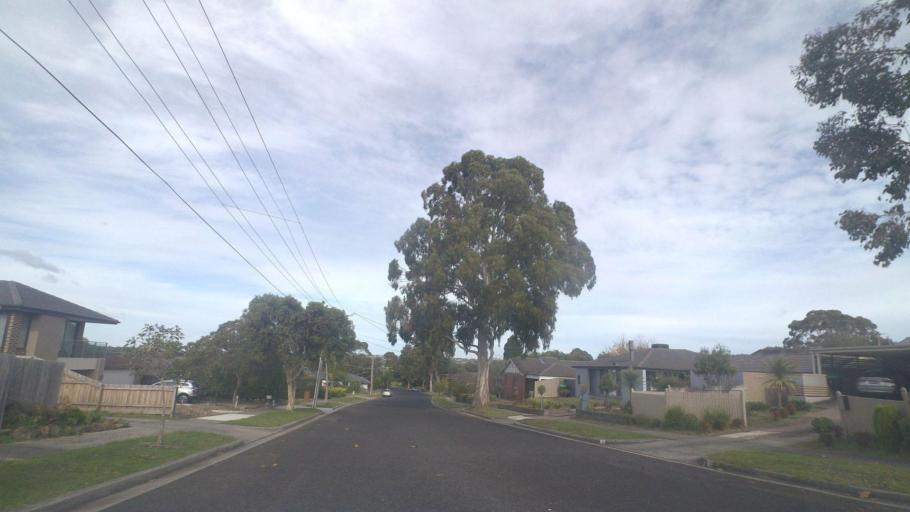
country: AU
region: Victoria
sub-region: Whitehorse
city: Vermont South
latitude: -37.8609
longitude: 145.1858
